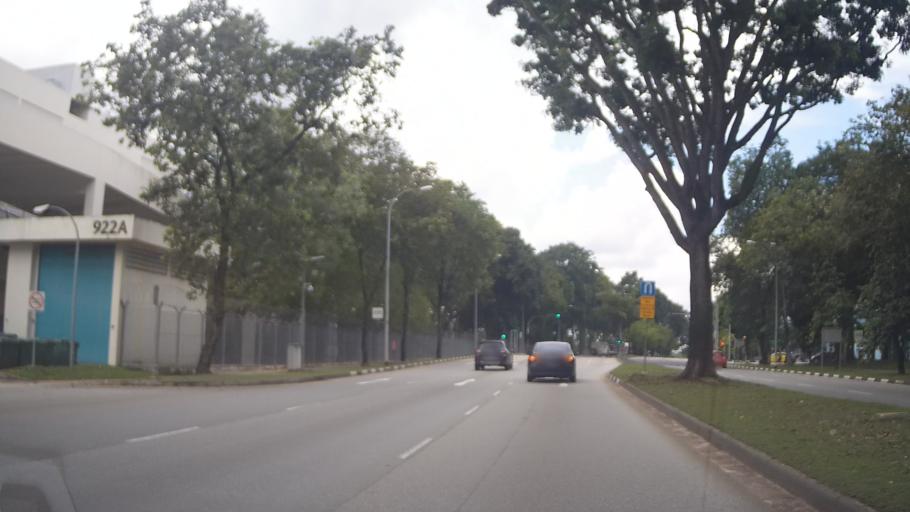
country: MY
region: Johor
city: Johor Bahru
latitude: 1.4006
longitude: 103.7427
